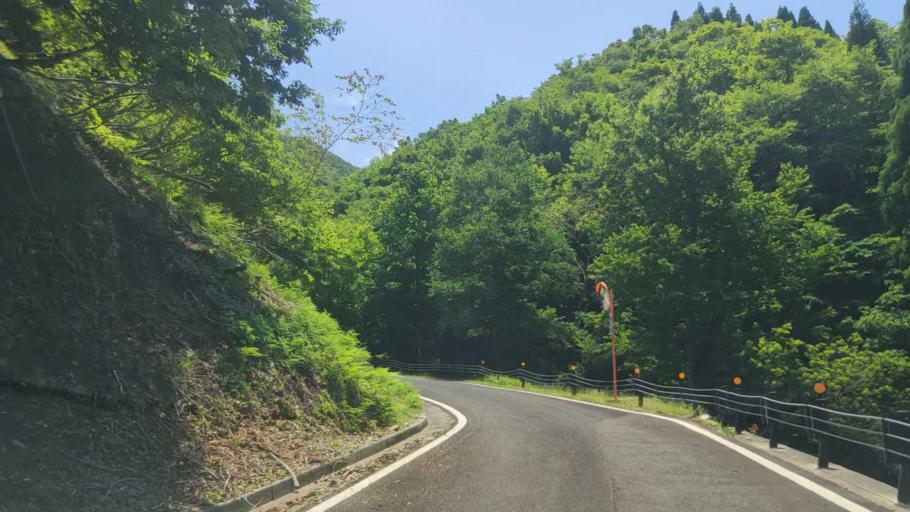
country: JP
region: Tottori
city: Tottori
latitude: 35.3734
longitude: 134.4913
